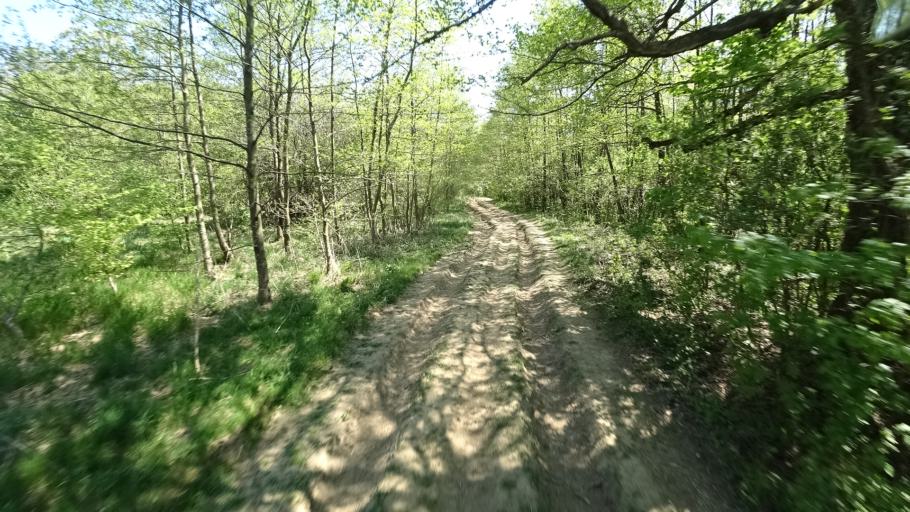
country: HR
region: Zagrebacka
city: Jablanovec
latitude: 45.8534
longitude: 15.8793
